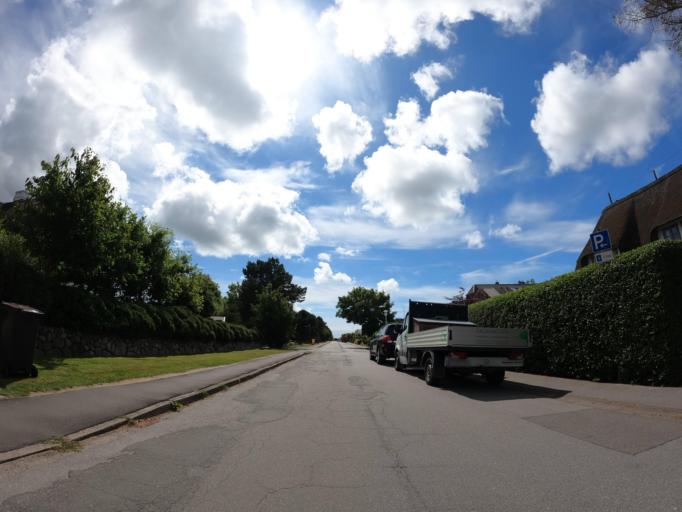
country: DE
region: Schleswig-Holstein
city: Keitum
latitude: 54.8939
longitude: 8.3648
